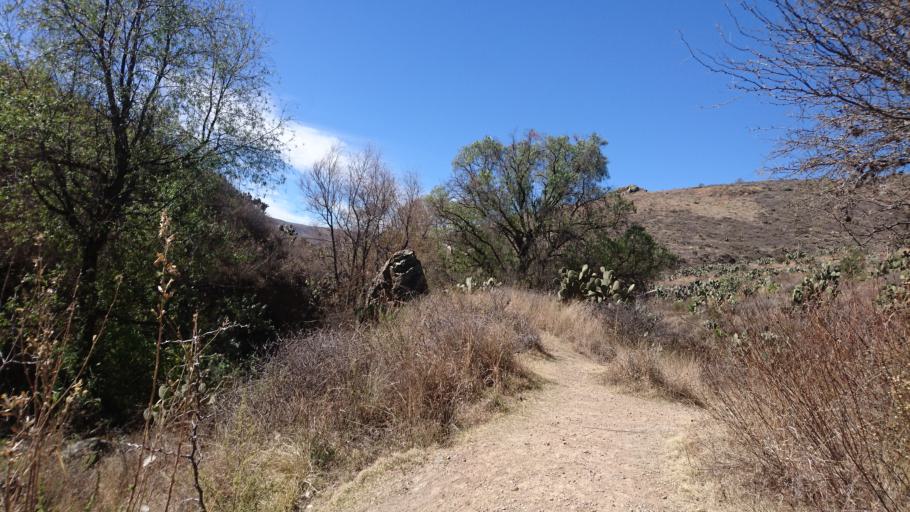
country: MX
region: Zacatecas
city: Guadalupe
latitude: 22.7792
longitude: -102.5444
